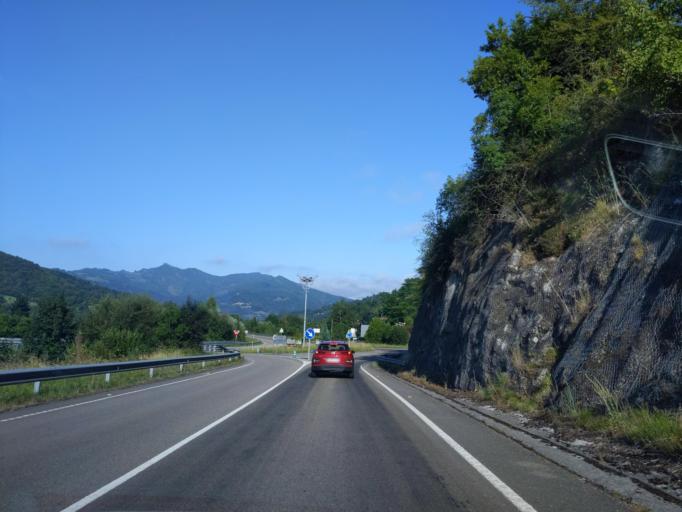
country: ES
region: Asturias
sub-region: Province of Asturias
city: Pola de Laviana
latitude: 43.2350
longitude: -5.5220
